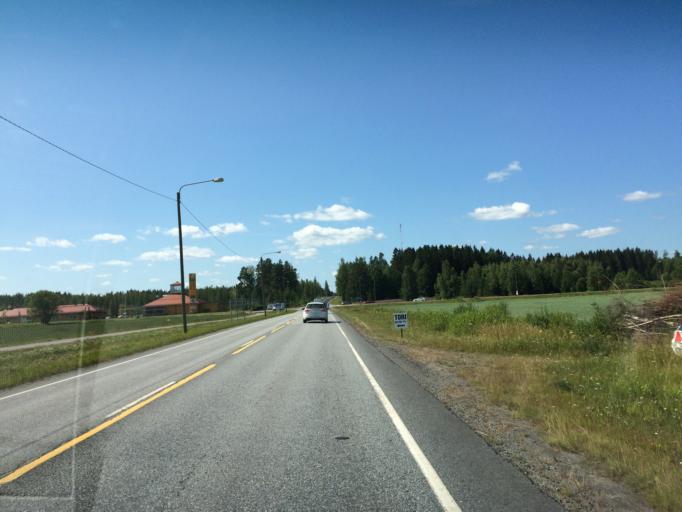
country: FI
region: Pirkanmaa
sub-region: Lounais-Pirkanmaa
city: Kiikoinen
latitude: 61.4755
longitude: 22.5619
